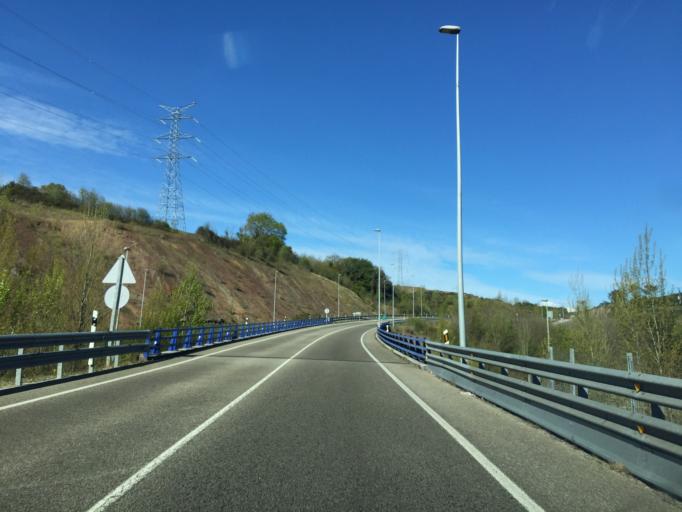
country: ES
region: Asturias
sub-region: Province of Asturias
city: Llanera
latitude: 43.3640
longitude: -5.9498
